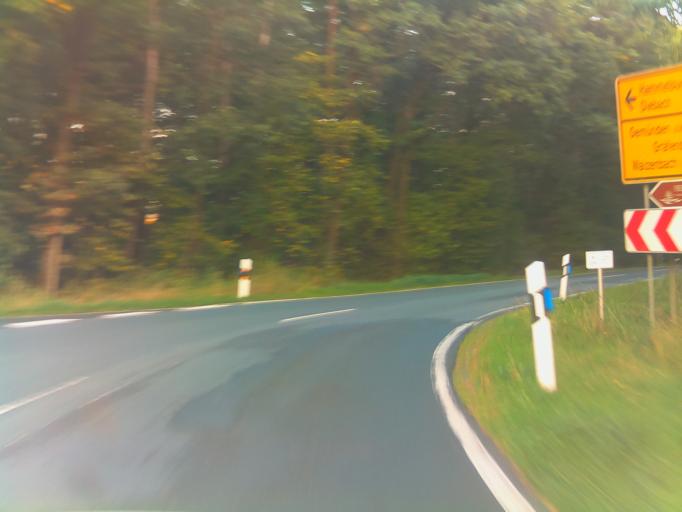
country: DE
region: Bavaria
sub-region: Regierungsbezirk Unterfranken
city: Wartmannsroth
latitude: 50.1513
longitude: 9.8038
